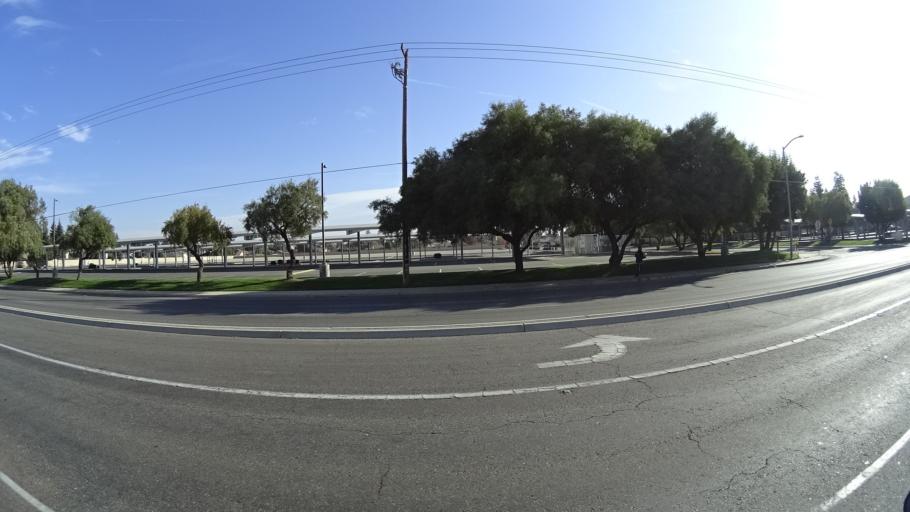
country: US
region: California
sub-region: Kern County
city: Greenacres
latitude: 35.4059
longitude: -119.0745
